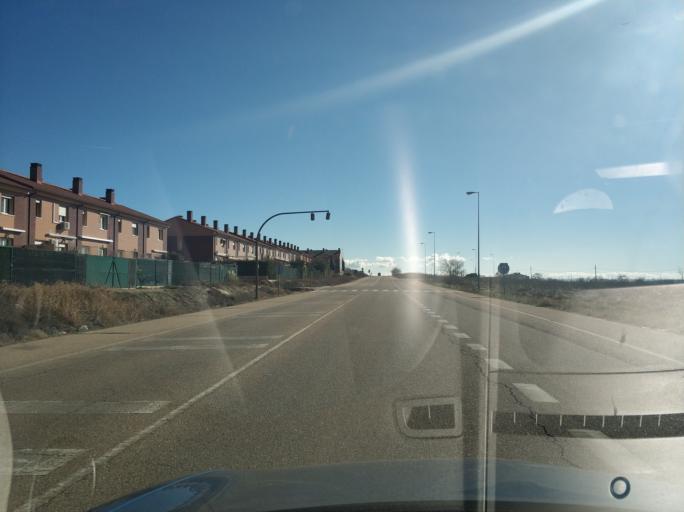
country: ES
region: Castille and Leon
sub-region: Provincia de Valladolid
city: Cisterniga
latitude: 41.6070
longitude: -4.6817
